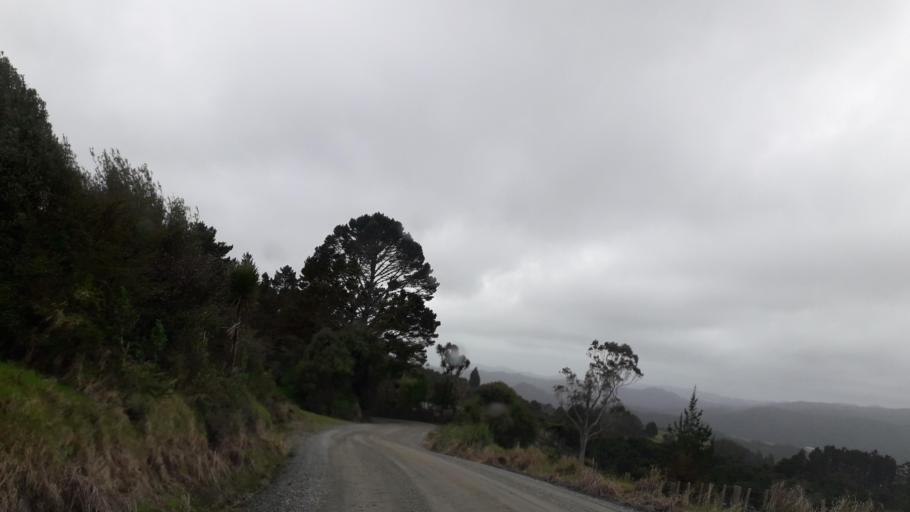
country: NZ
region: Northland
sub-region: Far North District
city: Kerikeri
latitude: -35.1228
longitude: 173.7473
